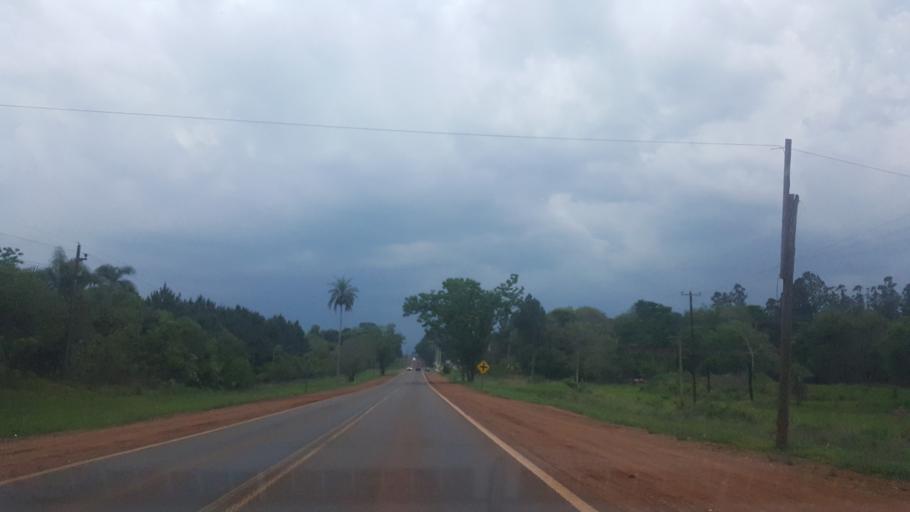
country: AR
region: Misiones
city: Gobernador Roca
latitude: -27.1764
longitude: -55.4534
